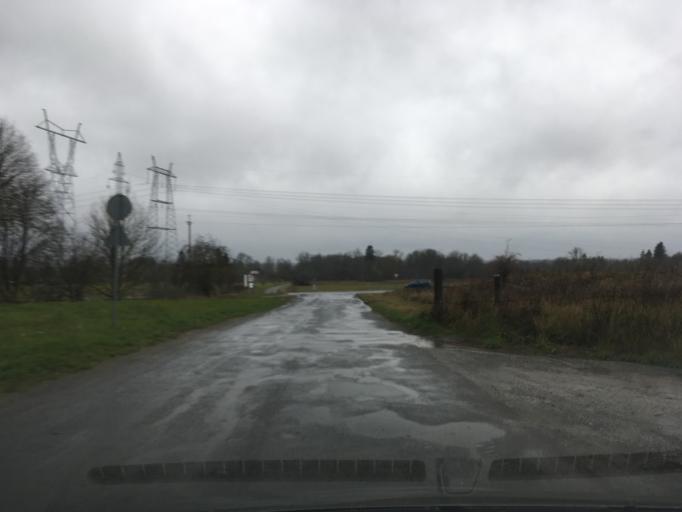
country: EE
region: Laeaene
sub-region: Lihula vald
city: Lihula
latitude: 58.6755
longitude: 23.8213
